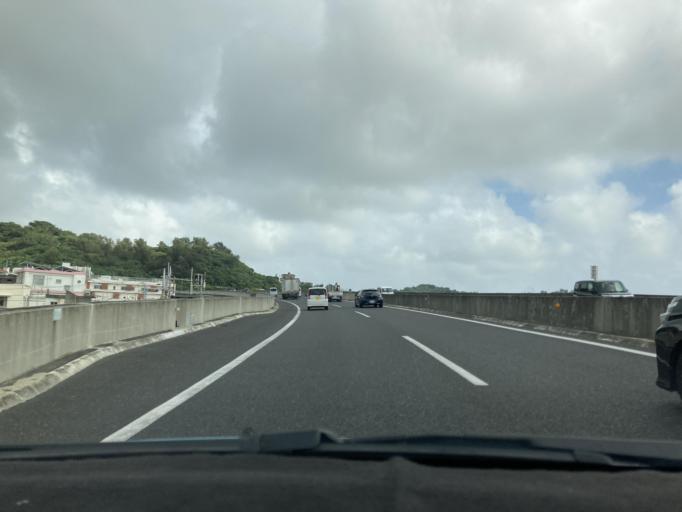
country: JP
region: Okinawa
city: Tomigusuku
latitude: 26.1725
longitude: 127.6766
